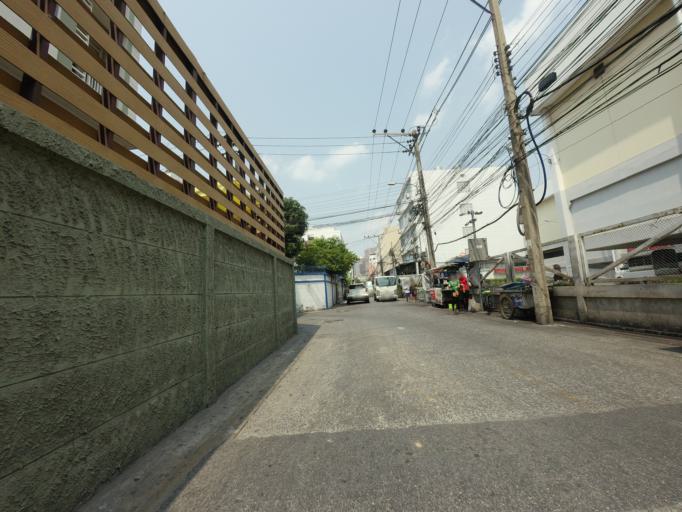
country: TH
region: Bangkok
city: Huai Khwang
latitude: 13.7702
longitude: 100.5708
